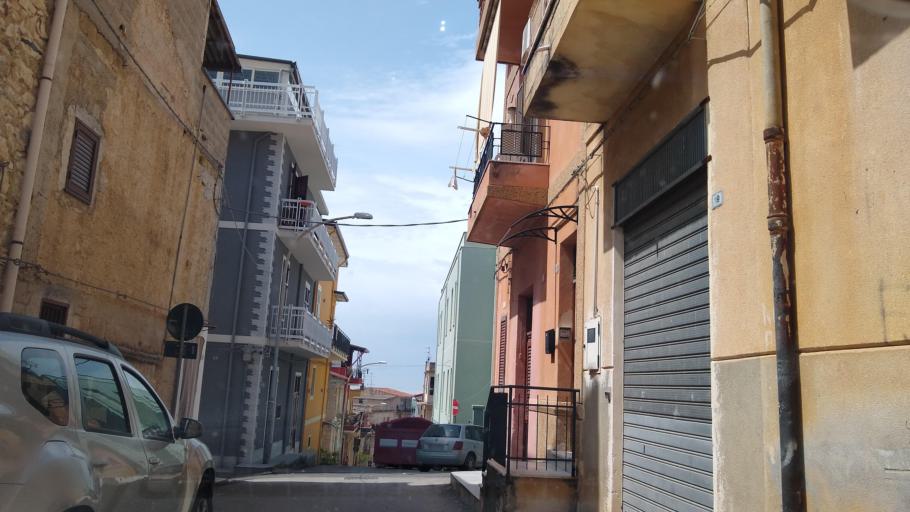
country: IT
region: Sicily
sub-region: Palermo
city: San Cipirello
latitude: 37.9630
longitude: 13.1747
